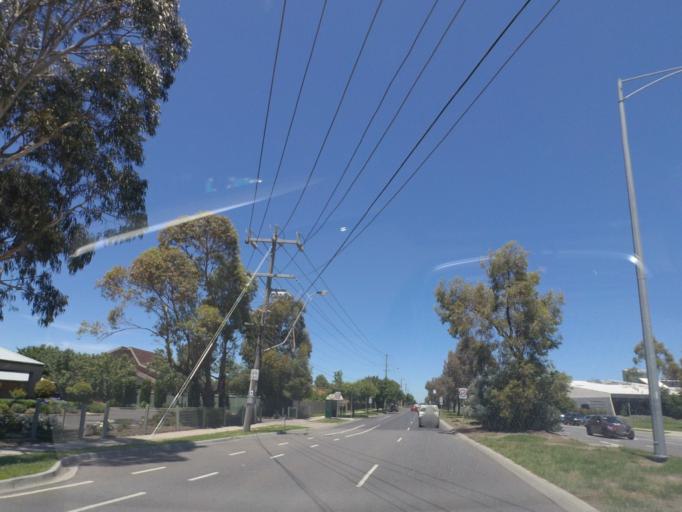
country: AU
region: Victoria
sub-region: Whittlesea
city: Epping
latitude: -37.6529
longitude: 145.0317
